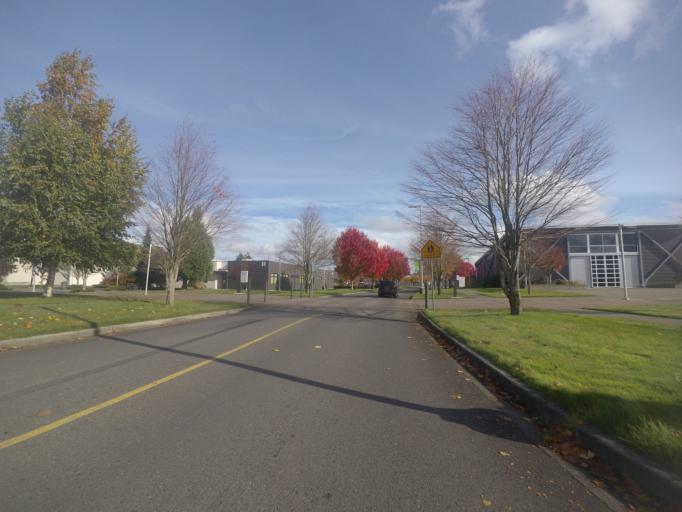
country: US
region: Washington
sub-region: Pierce County
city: Lakewood
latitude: 47.1742
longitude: -122.4942
